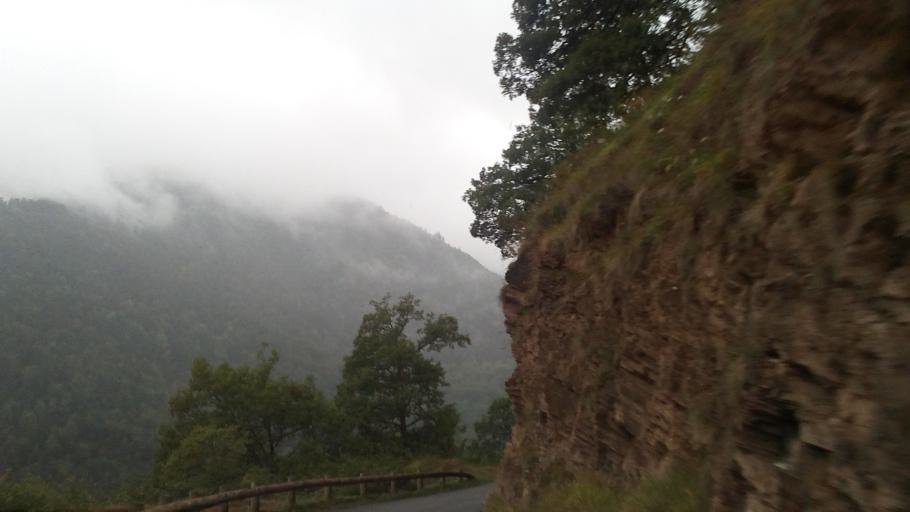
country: FR
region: Midi-Pyrenees
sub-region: Departement des Hautes-Pyrenees
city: Saint-Lary-Soulan
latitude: 42.8801
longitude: 0.3315
